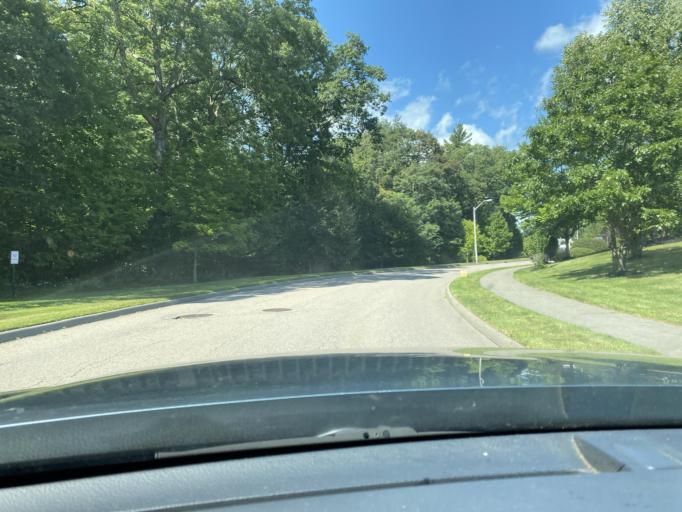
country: US
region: Massachusetts
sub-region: Norfolk County
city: Norwood
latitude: 42.1651
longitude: -71.2194
